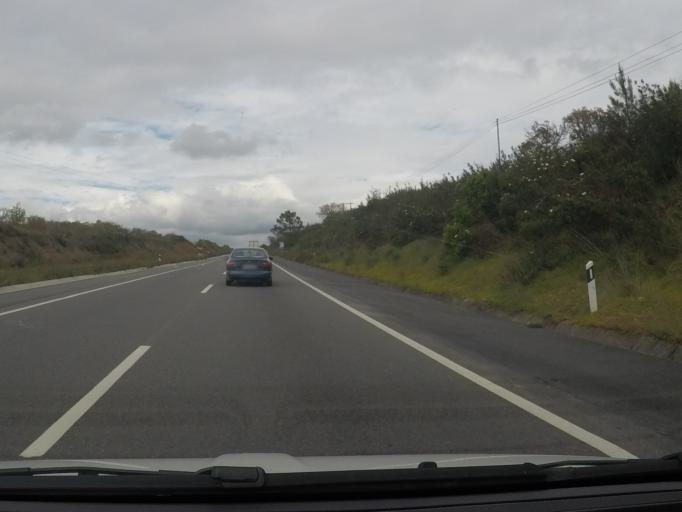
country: PT
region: Setubal
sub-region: Santiago do Cacem
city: Santiago do Cacem
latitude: 38.0672
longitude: -8.6918
